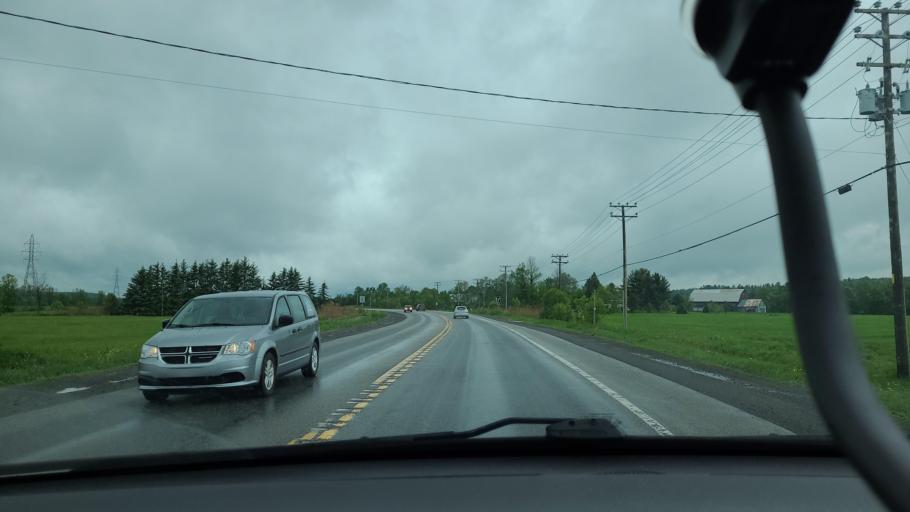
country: CA
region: Quebec
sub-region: Laurentides
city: Saint-Jerome
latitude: 45.7457
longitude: -74.0198
